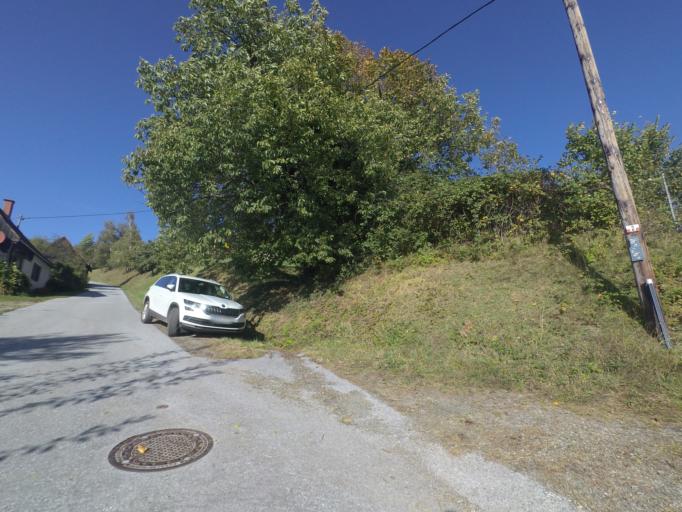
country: AT
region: Styria
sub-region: Politischer Bezirk Leibnitz
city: Kitzeck im Sausal
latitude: 46.7792
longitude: 15.4331
